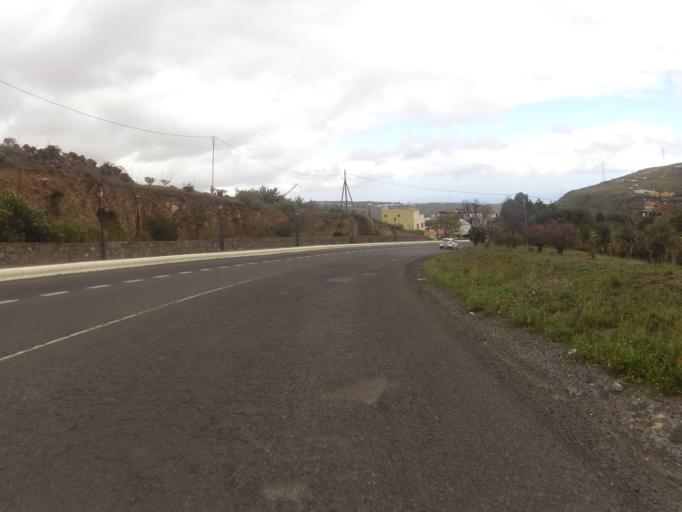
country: ES
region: Canary Islands
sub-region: Provincia de Las Palmas
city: Valsequillo de Gran Canaria
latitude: 27.9964
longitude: -15.4671
